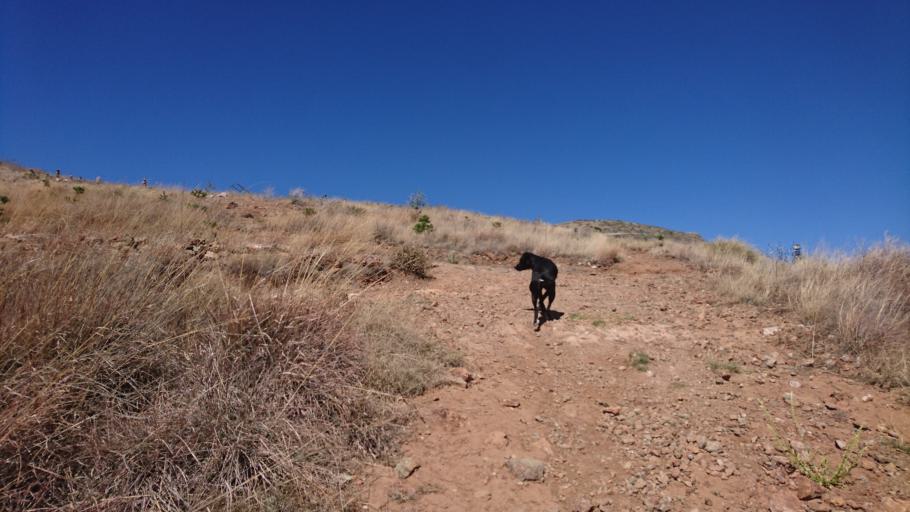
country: MX
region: Zacatecas
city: Zacatecas
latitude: 22.7768
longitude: -102.5471
